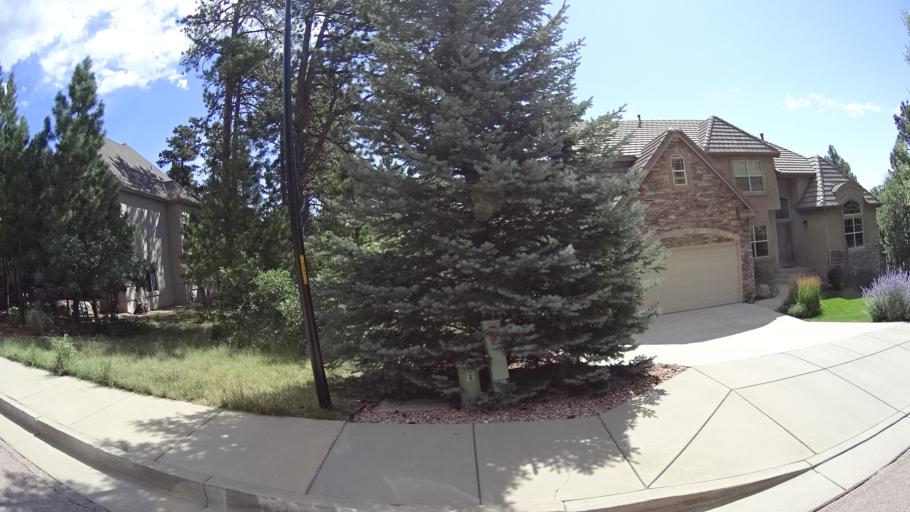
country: US
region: Colorado
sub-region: El Paso County
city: Fort Carson
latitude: 38.7504
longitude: -104.8420
